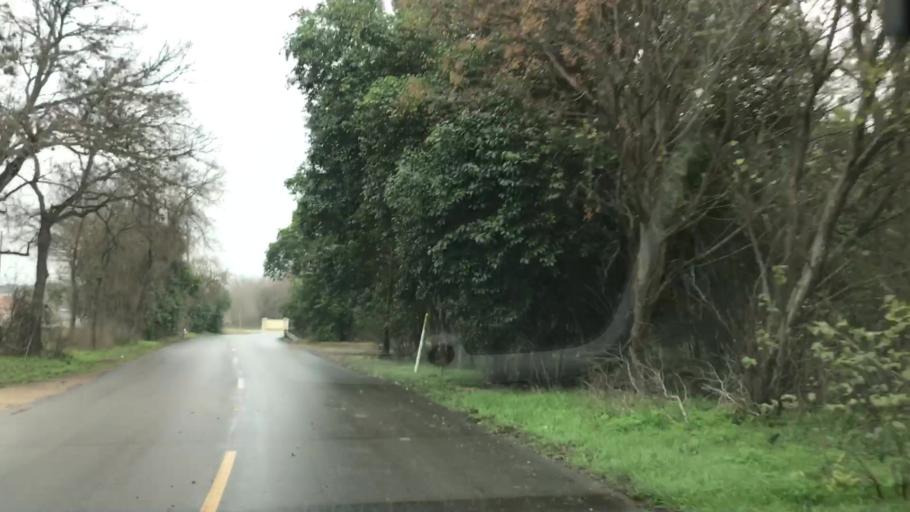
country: US
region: Texas
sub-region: Hays County
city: San Marcos
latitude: 29.8862
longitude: -97.9068
